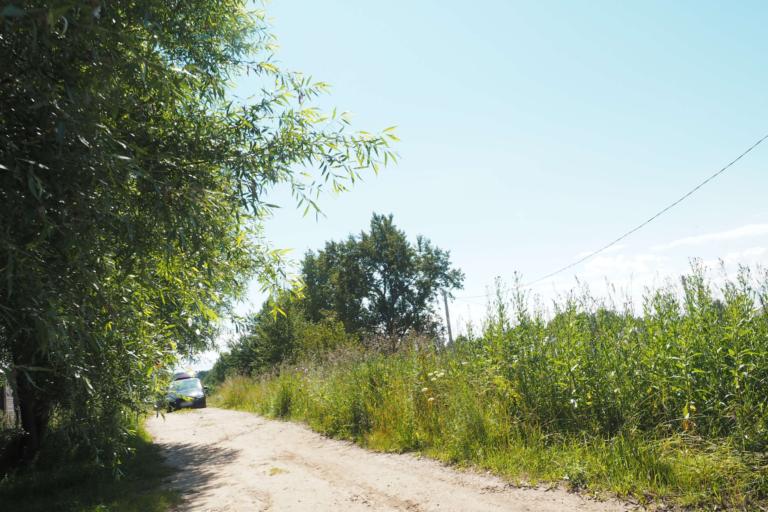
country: RU
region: Moskovskaya
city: Ramenskoye
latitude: 55.5730
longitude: 38.2973
